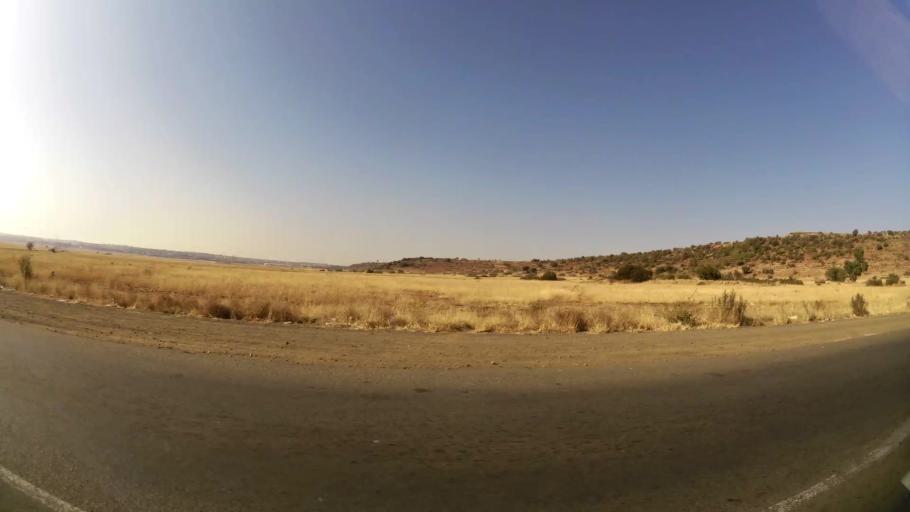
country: ZA
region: Orange Free State
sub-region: Mangaung Metropolitan Municipality
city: Bloemfontein
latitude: -29.1726
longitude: 26.1996
